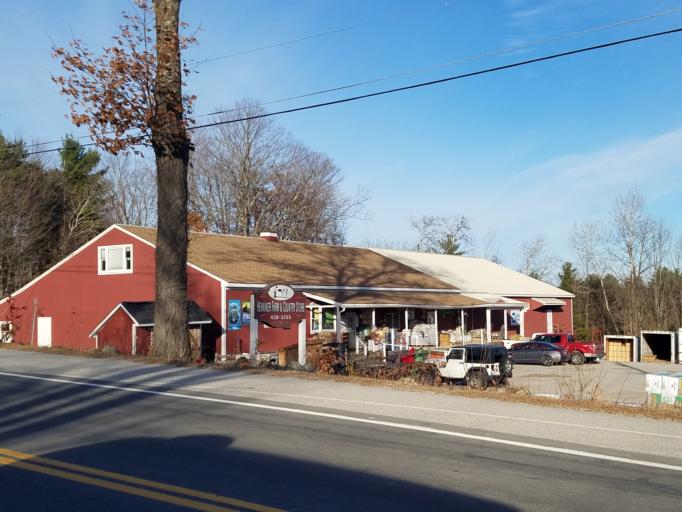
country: US
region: New Hampshire
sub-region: Merrimack County
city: Henniker
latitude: 43.1909
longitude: -71.8287
